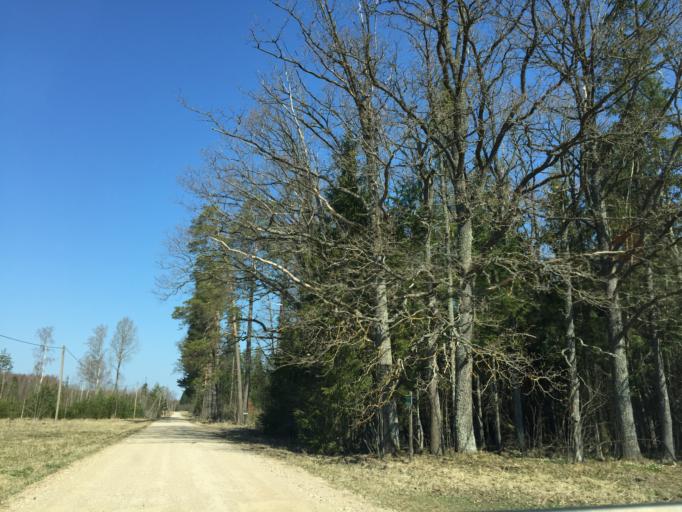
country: EE
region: Tartu
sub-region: Alatskivi vald
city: Kallaste
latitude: 58.5386
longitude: 26.9451
